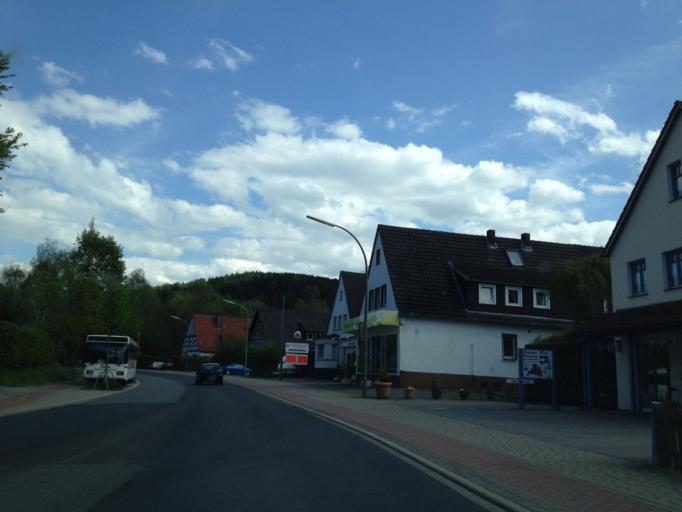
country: DE
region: North Rhine-Westphalia
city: Warstein
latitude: 51.4816
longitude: 8.2513
